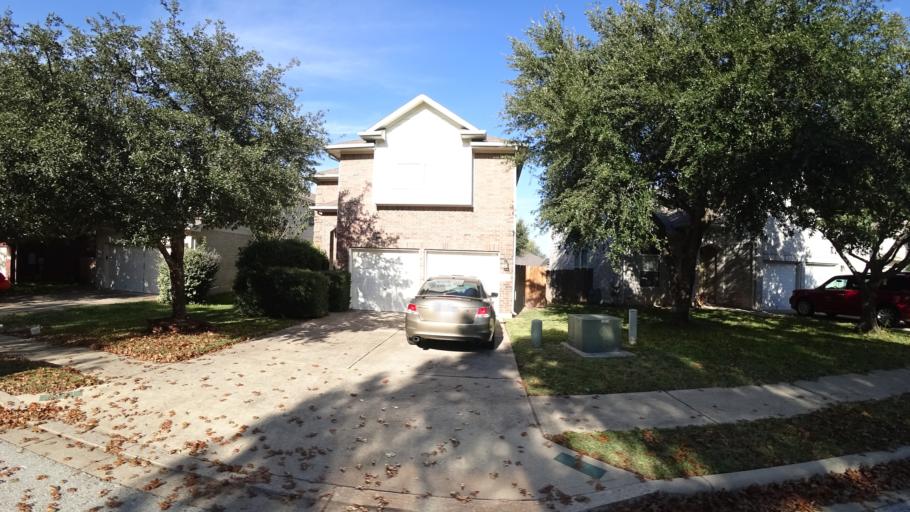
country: US
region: Texas
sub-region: Travis County
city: Wells Branch
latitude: 30.4612
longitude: -97.6808
